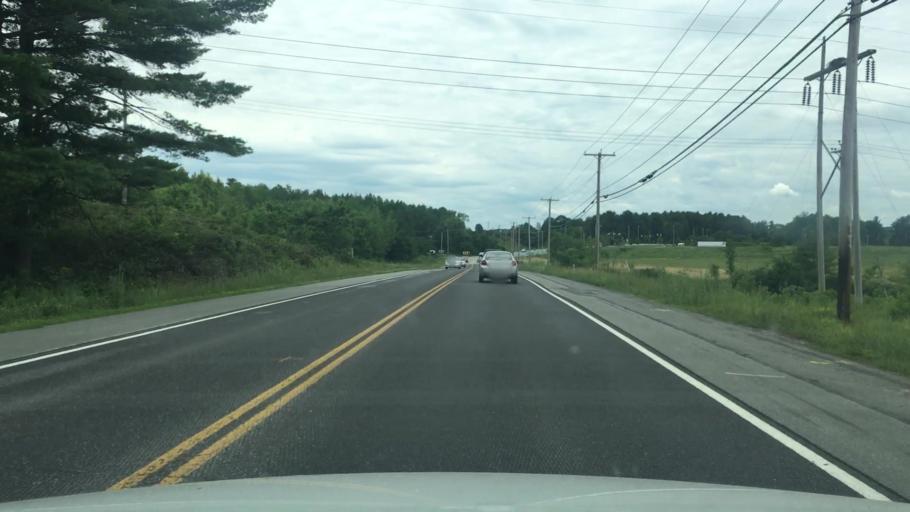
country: US
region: Maine
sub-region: Kennebec County
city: Augusta
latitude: 44.3284
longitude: -69.7383
